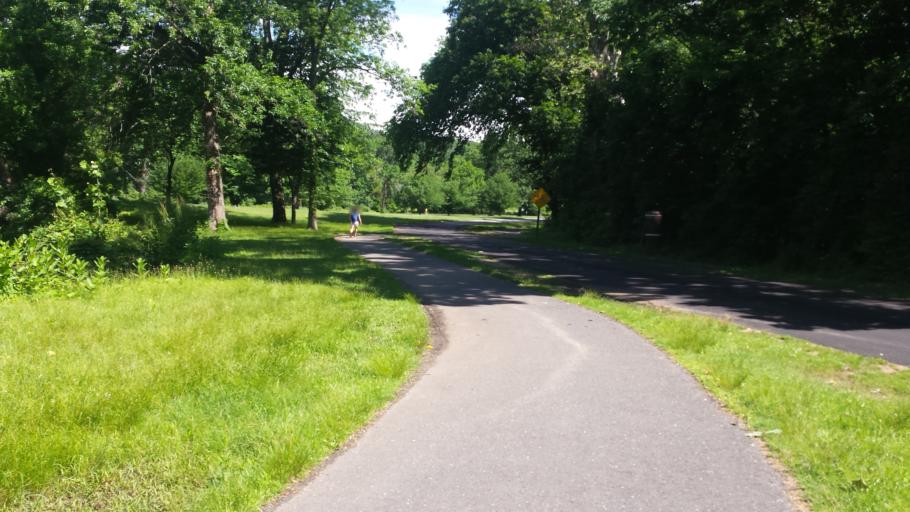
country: US
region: New York
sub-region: Westchester County
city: White Plains
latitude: 41.0390
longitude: -73.7767
